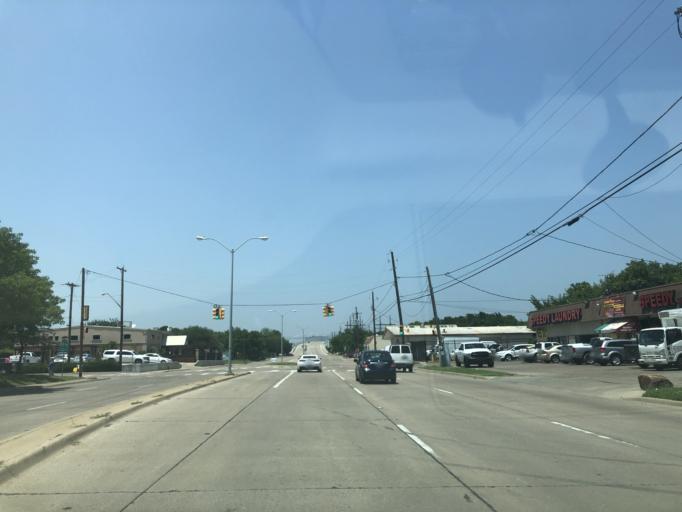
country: US
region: Texas
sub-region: Dallas County
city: Dallas
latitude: 32.7808
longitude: -96.8358
